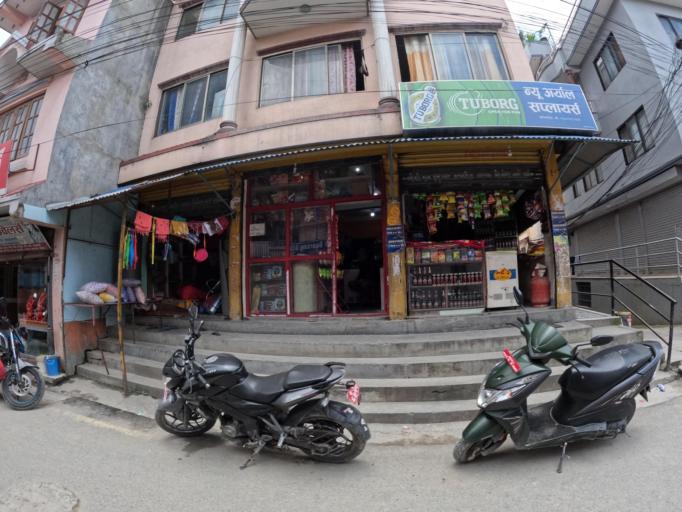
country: NP
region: Central Region
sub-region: Bagmati Zone
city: Kathmandu
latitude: 27.7485
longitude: 85.3175
